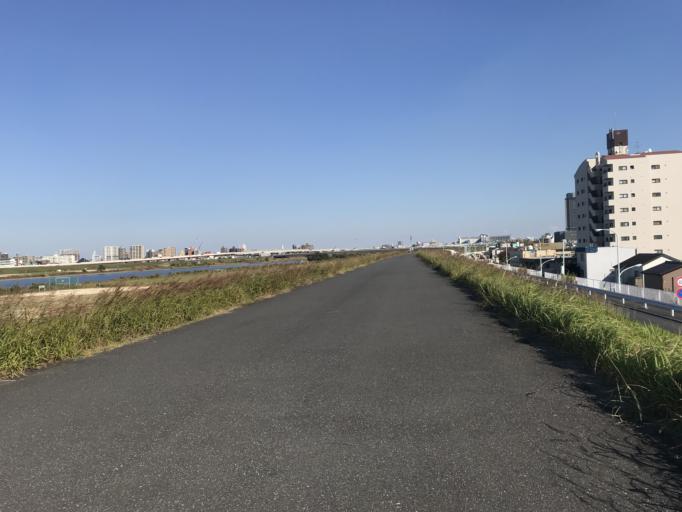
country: JP
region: Saitama
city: Soka
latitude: 35.7563
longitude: 139.7918
